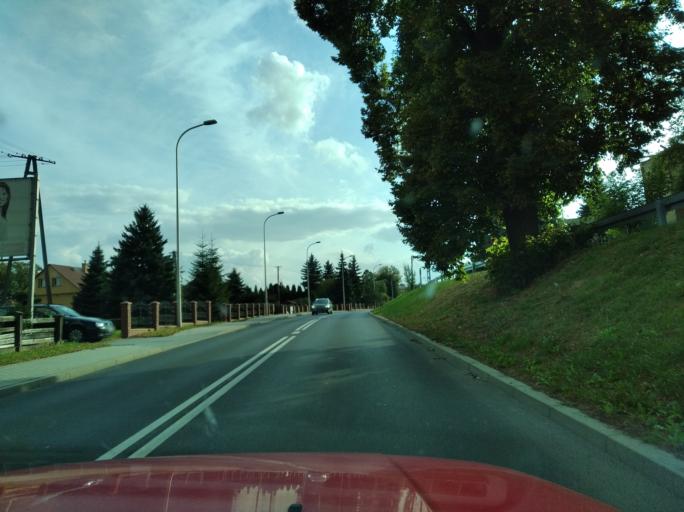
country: PL
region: Subcarpathian Voivodeship
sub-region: Powiat jaroslawski
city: Jaroslaw
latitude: 50.0041
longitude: 22.6746
